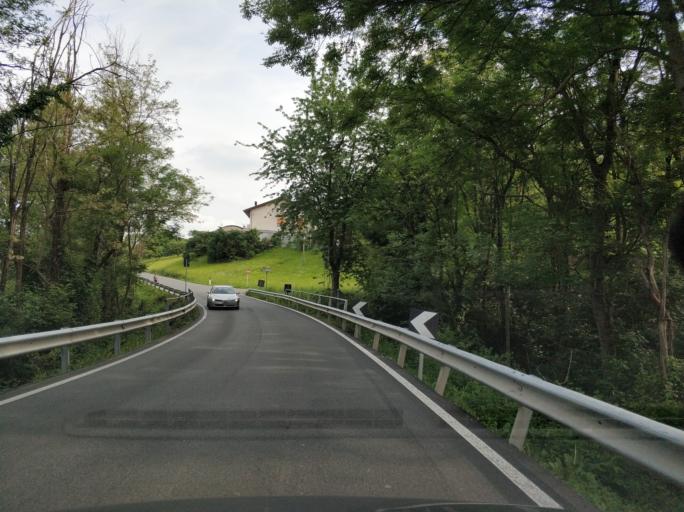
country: IT
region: Piedmont
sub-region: Provincia di Torino
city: Corio
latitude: 45.2971
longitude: 7.5460
